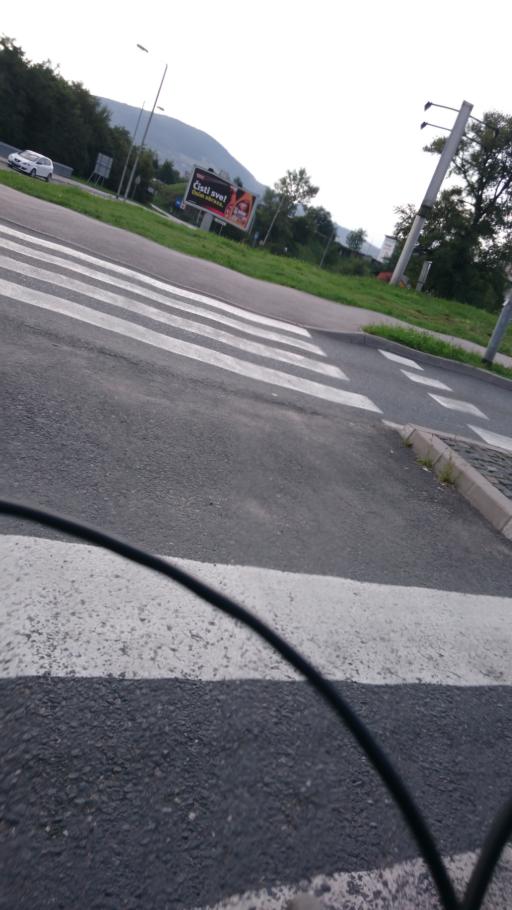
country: BA
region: Federation of Bosnia and Herzegovina
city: Zenica
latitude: 44.1970
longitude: 17.9242
